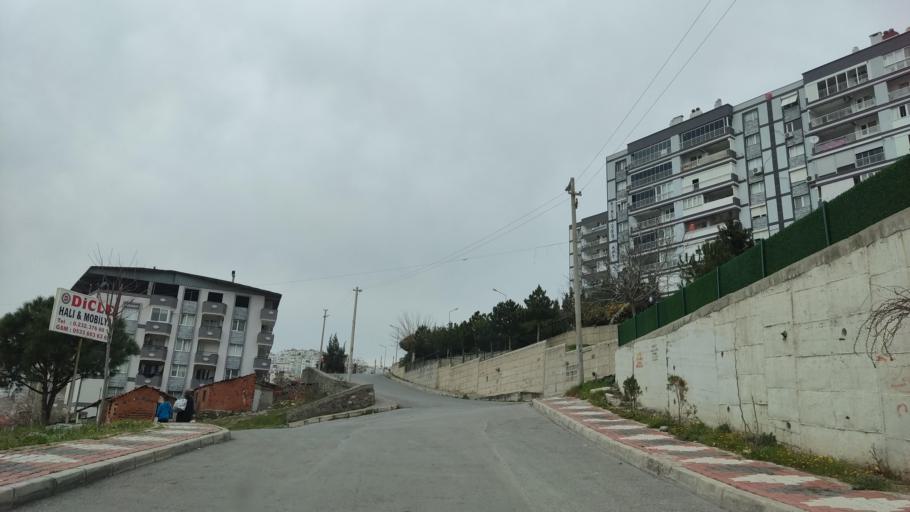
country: TR
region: Izmir
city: Karsiyaka
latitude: 38.5020
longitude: 27.0718
